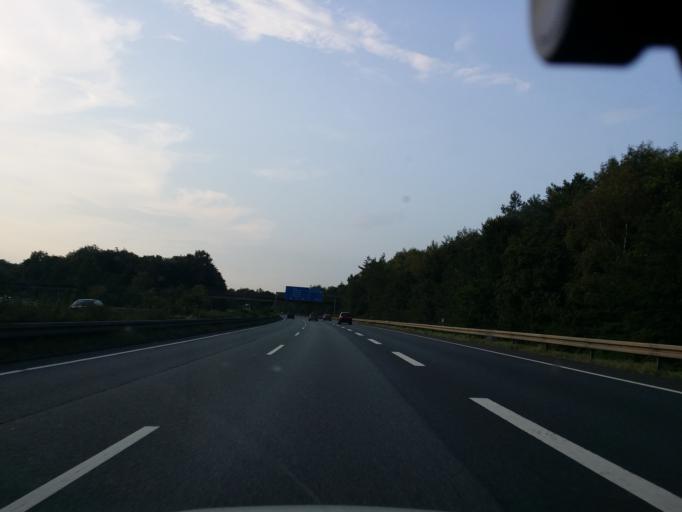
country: DE
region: Hesse
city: Raunheim
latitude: 50.0177
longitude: 8.4971
